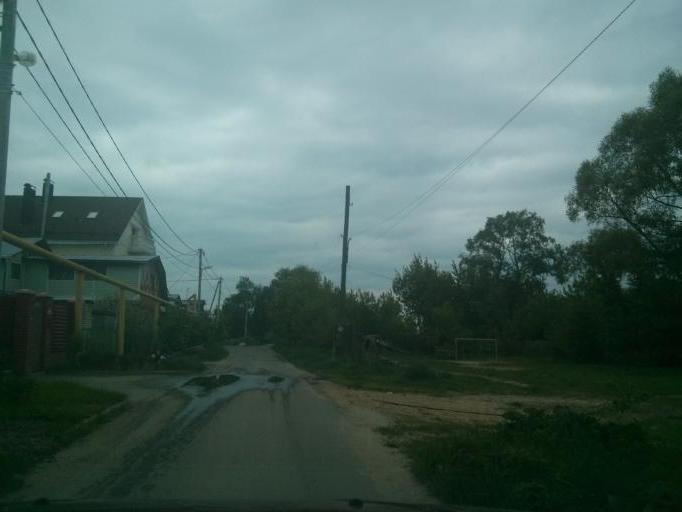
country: RU
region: Nizjnij Novgorod
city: Afonino
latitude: 56.3042
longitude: 44.0976
